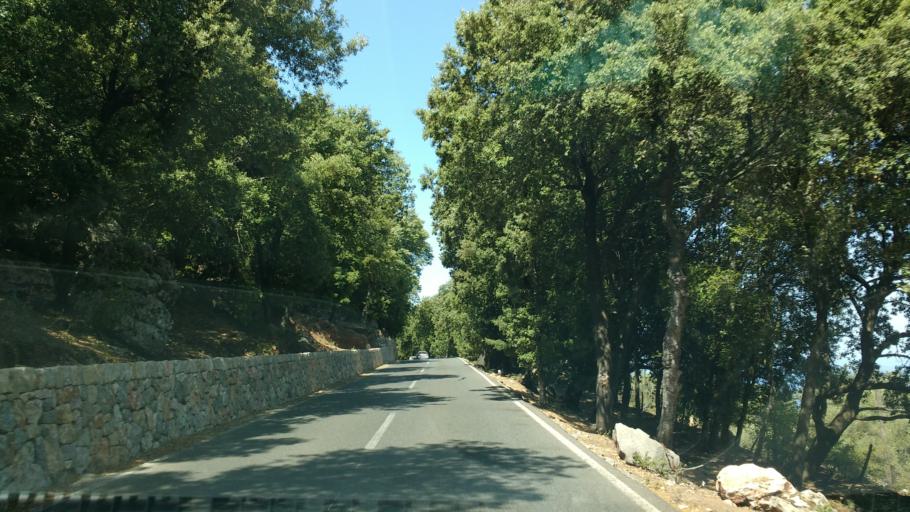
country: ES
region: Balearic Islands
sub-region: Illes Balears
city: Escorca
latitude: 39.8263
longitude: 2.8456
